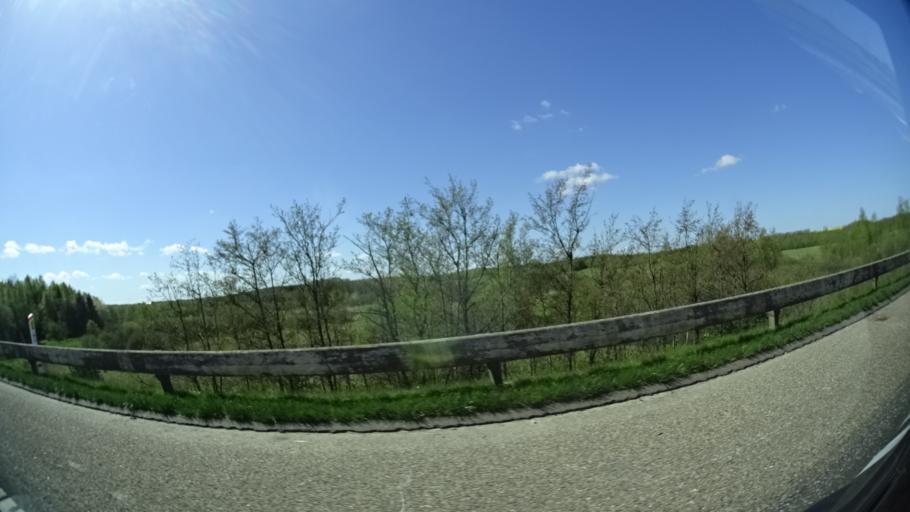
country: DK
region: Central Jutland
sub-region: Favrskov Kommune
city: Hadsten
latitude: 56.3183
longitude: 10.1194
